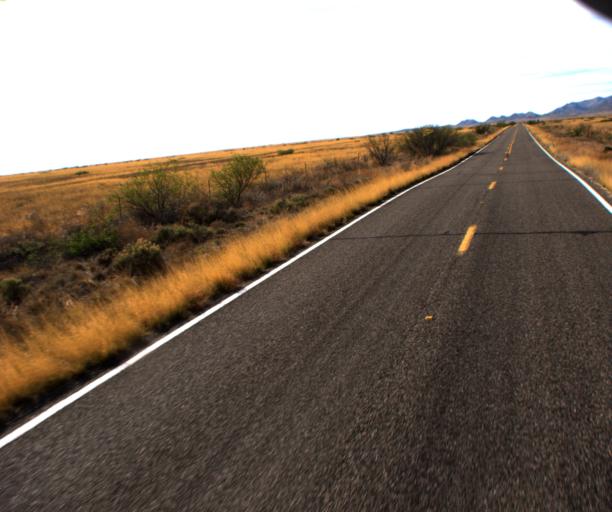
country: US
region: Arizona
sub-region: Cochise County
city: Willcox
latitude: 32.0811
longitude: -109.5218
